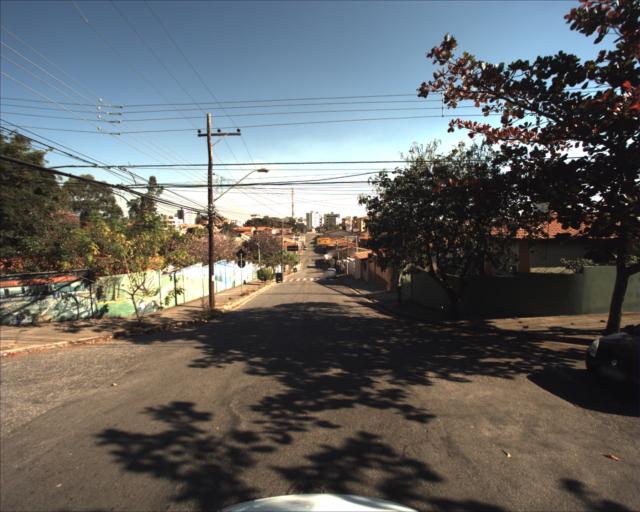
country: BR
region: Sao Paulo
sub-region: Sorocaba
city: Sorocaba
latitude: -23.5063
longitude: -47.4245
